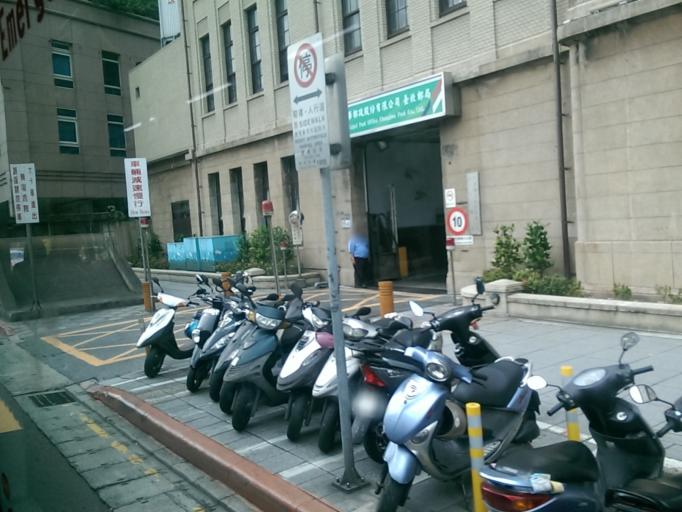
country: TW
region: Taipei
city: Taipei
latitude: 25.0472
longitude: 121.5118
